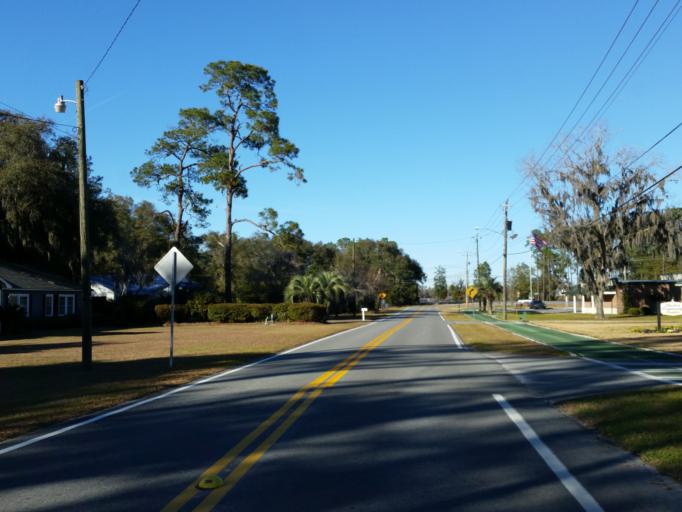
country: US
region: Georgia
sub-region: Lowndes County
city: Valdosta
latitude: 30.7507
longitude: -83.2188
